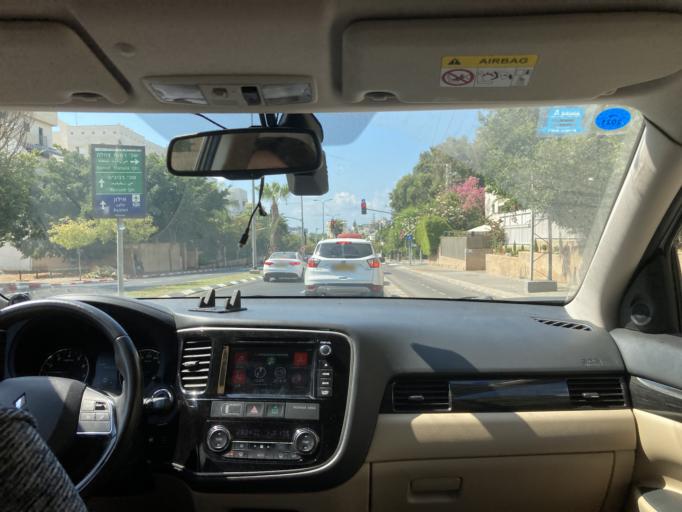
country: IL
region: Tel Aviv
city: Ramat HaSharon
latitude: 32.1189
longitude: 34.8300
